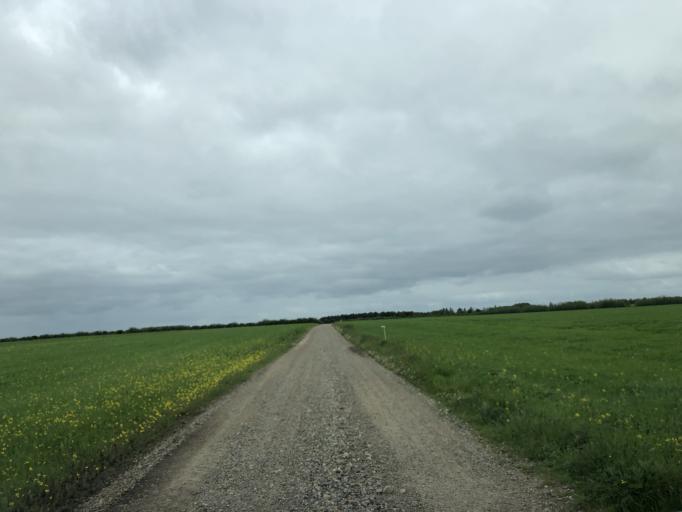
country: DK
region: Central Jutland
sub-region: Holstebro Kommune
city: Ulfborg
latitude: 56.2276
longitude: 8.1818
